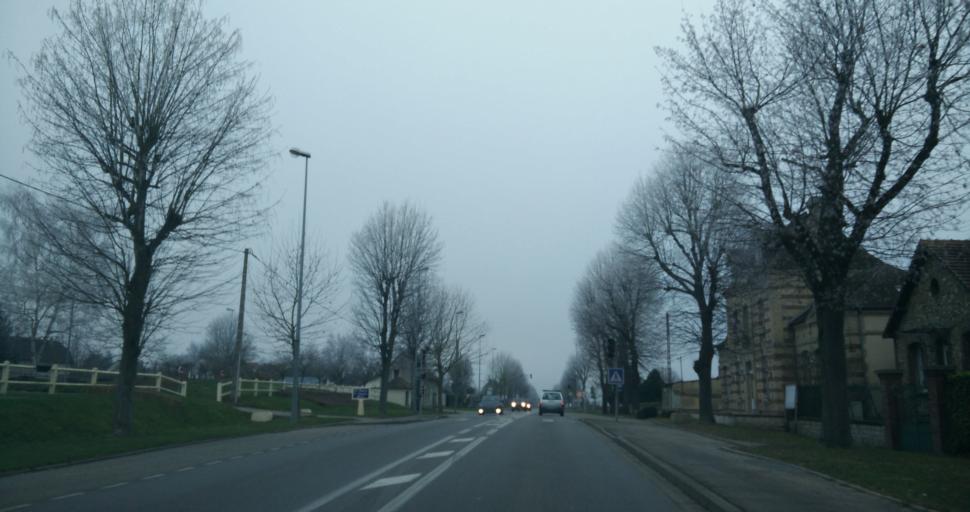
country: FR
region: Haute-Normandie
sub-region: Departement de l'Eure
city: La Chapelle-Reanville
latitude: 49.1463
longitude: 1.3981
